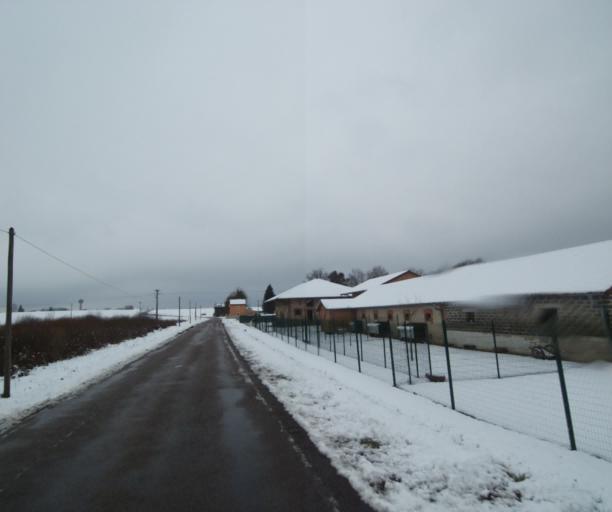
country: FR
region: Champagne-Ardenne
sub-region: Departement de la Haute-Marne
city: Laneuville-a-Remy
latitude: 48.5109
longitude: 4.8476
